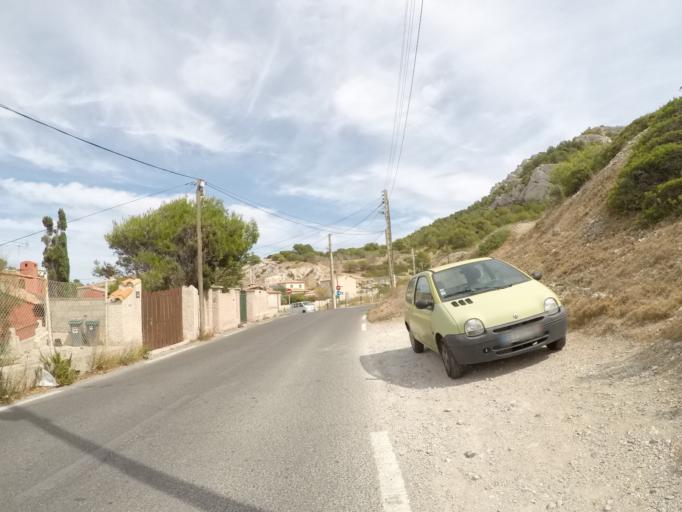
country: FR
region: Provence-Alpes-Cote d'Azur
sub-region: Departement des Bouches-du-Rhone
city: Marseille 08
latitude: 43.2279
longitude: 5.3512
